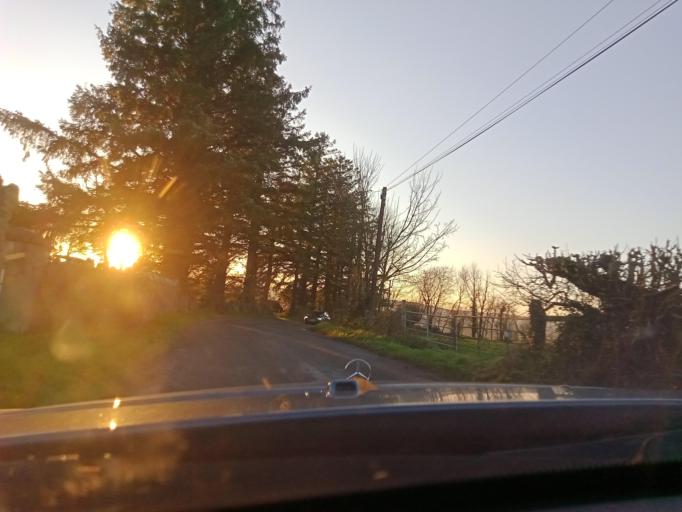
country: IE
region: Munster
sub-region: Waterford
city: Waterford
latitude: 52.3682
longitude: -7.1586
